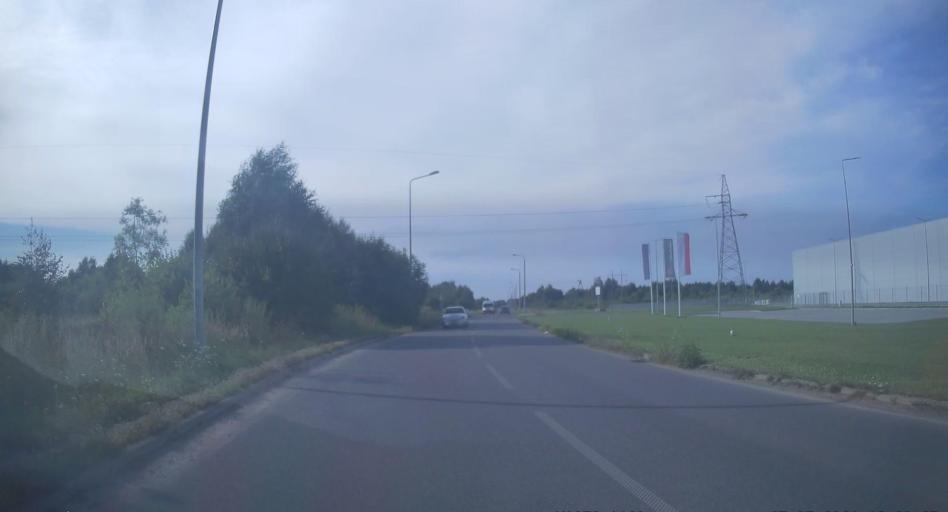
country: PL
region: Swietokrzyskie
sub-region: Powiat konecki
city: Konskie
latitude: 51.2080
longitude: 20.3972
